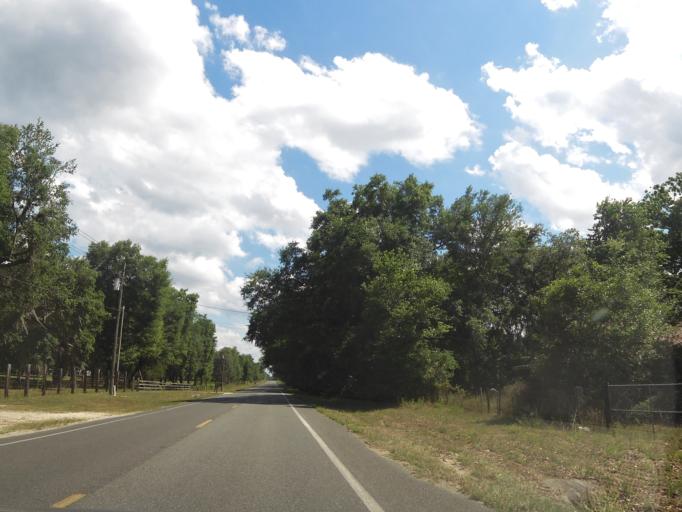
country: US
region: Florida
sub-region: Clay County
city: Keystone Heights
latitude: 29.8263
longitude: -81.9225
